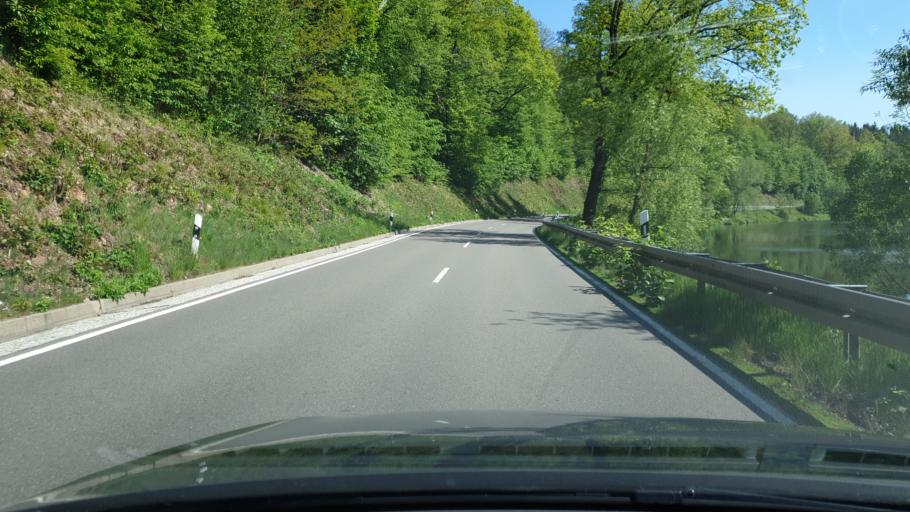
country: DE
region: Saxony
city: Mittweida
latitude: 50.9808
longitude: 13.0007
